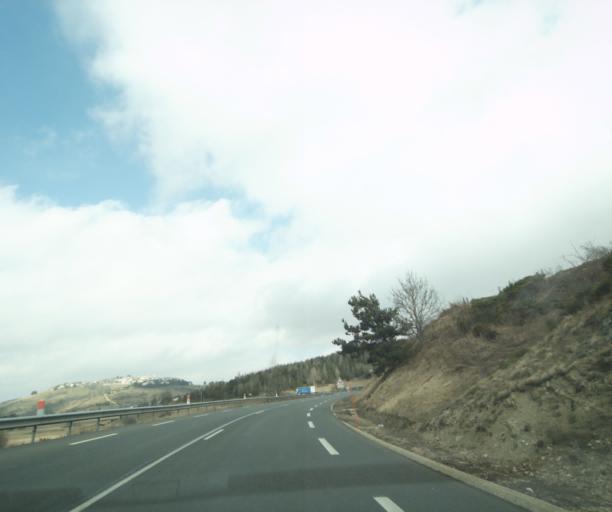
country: FR
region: Languedoc-Roussillon
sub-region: Departement de la Lozere
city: Mende
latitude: 44.6252
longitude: 3.6742
